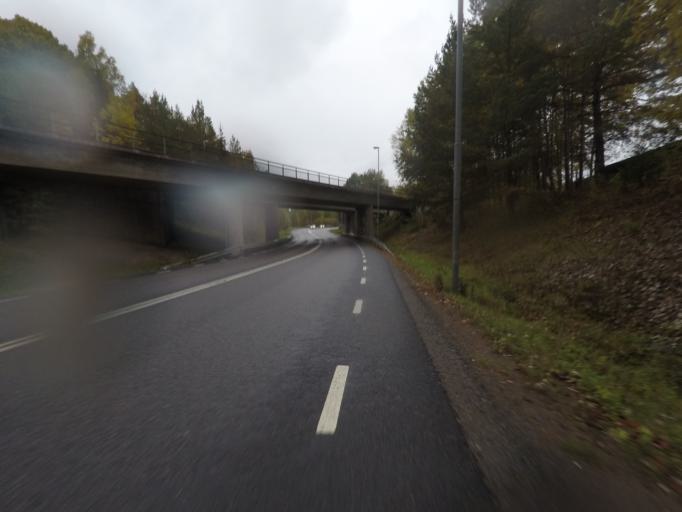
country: SE
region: OErebro
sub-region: Karlskoga Kommun
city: Karlskoga
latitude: 59.3178
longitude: 14.4724
